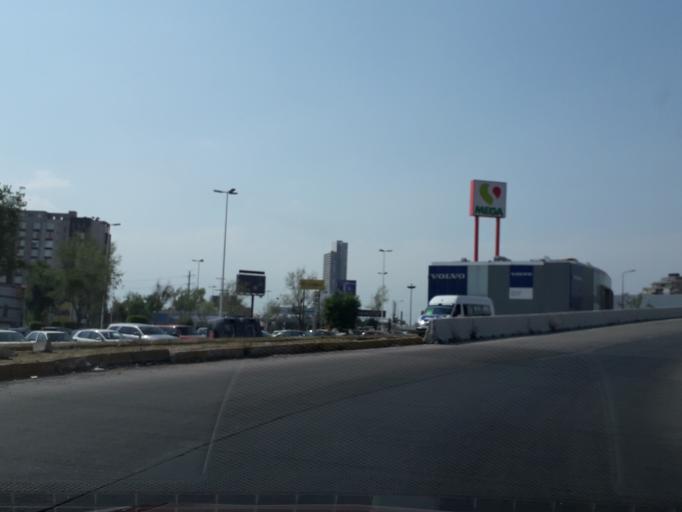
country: MX
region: Puebla
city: Puebla
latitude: 19.0286
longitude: -98.2341
